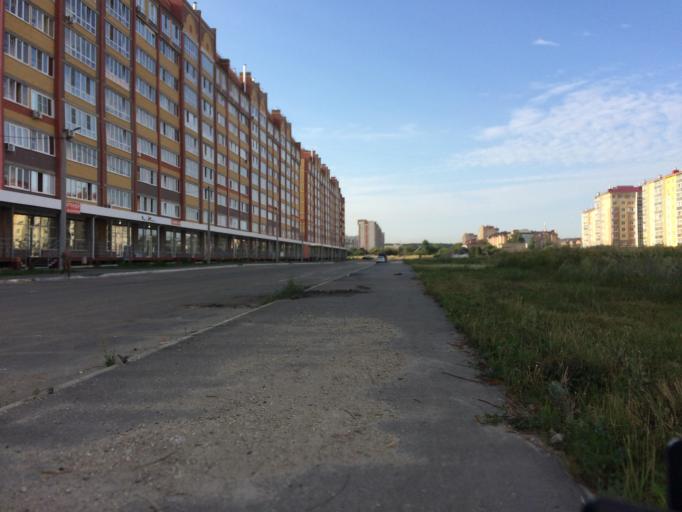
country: RU
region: Mariy-El
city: Medvedevo
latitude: 56.6382
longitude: 47.8191
